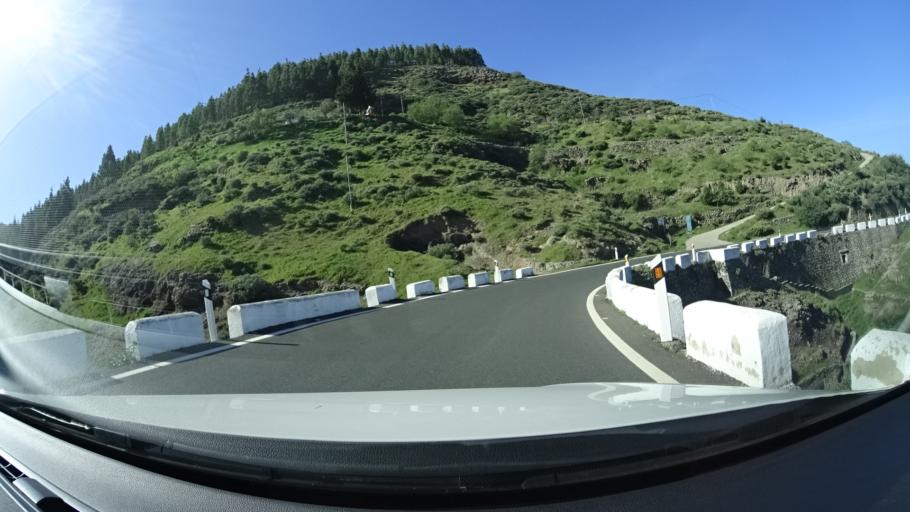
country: ES
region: Canary Islands
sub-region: Provincia de Las Palmas
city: Artenara
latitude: 28.0240
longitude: -15.6345
